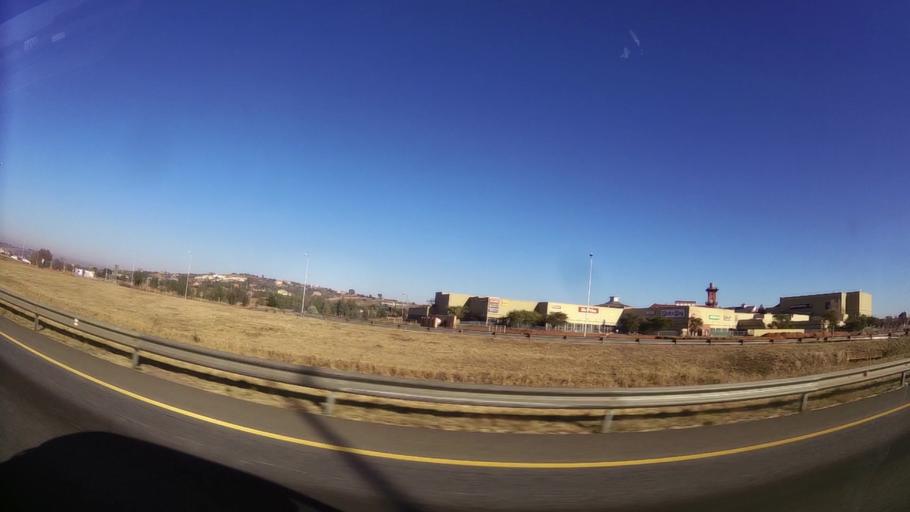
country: ZA
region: Gauteng
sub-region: City of Tshwane Metropolitan Municipality
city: Centurion
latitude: -25.8626
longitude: 28.2533
